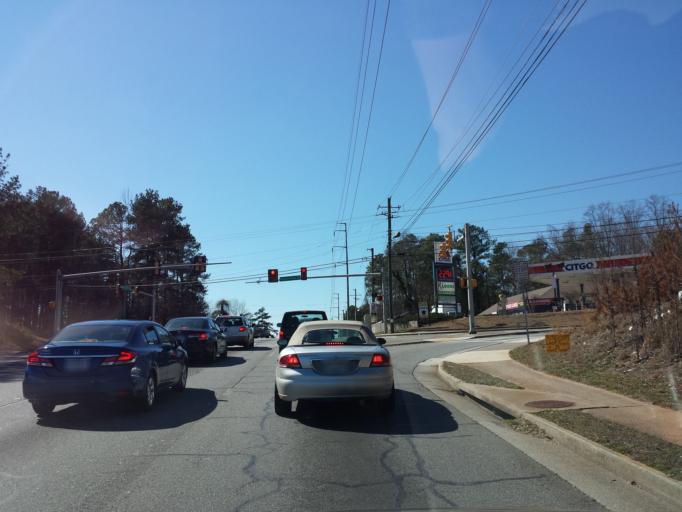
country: US
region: Georgia
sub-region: Cobb County
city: Fair Oaks
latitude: 33.8946
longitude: -84.5434
